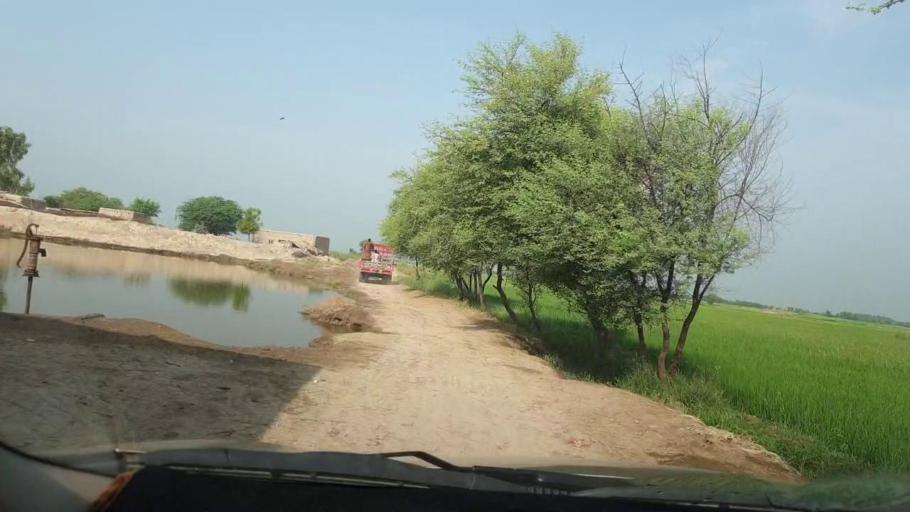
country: PK
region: Sindh
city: Goth Garelo
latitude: 27.4754
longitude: 68.0534
